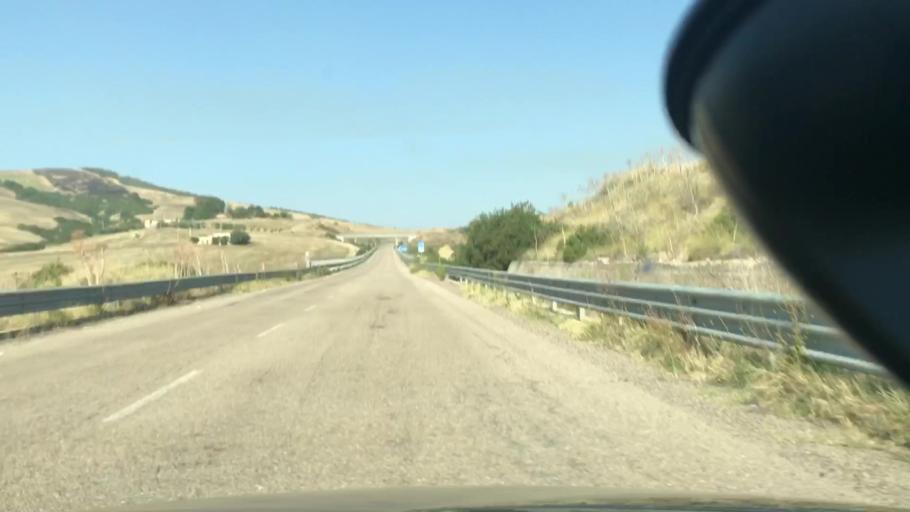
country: IT
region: Basilicate
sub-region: Provincia di Matera
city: La Martella
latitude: 40.6919
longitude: 16.4380
